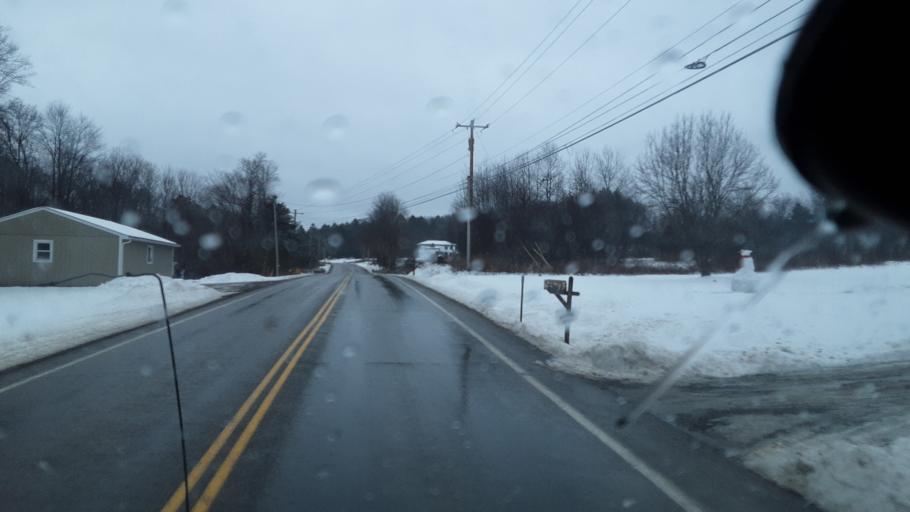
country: US
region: New York
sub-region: Allegany County
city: Andover
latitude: 42.0655
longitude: -77.8219
